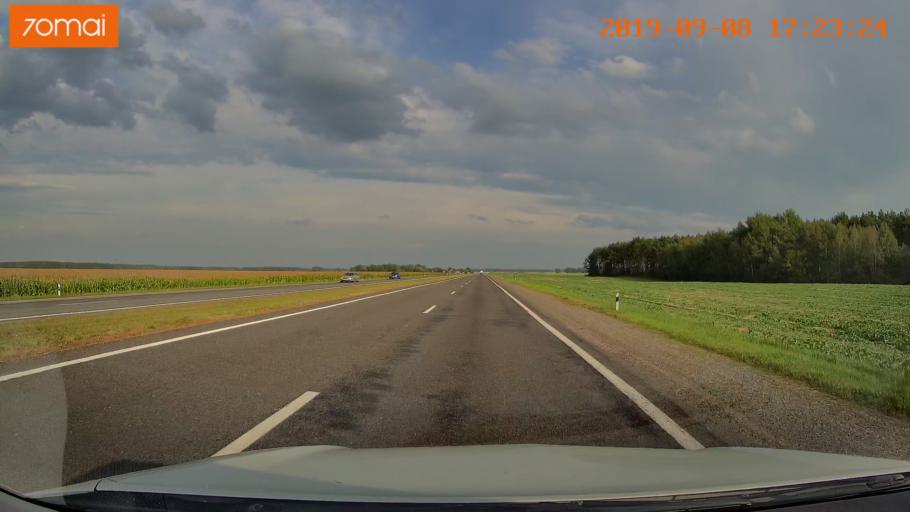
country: BY
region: Grodnenskaya
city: Skidal'
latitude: 53.5806
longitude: 24.2961
